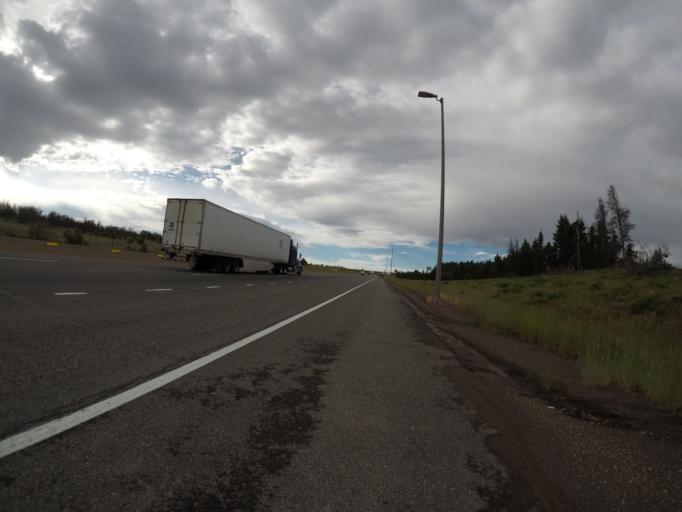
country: US
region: Wyoming
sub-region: Albany County
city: Laramie
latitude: 41.2458
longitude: -105.4417
